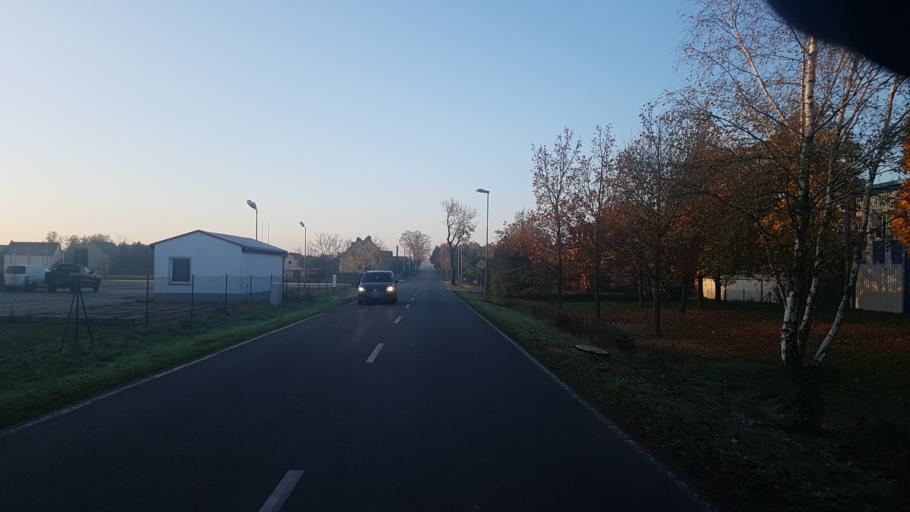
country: DE
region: Saxony
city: Torgau
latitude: 51.4977
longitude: 12.9921
